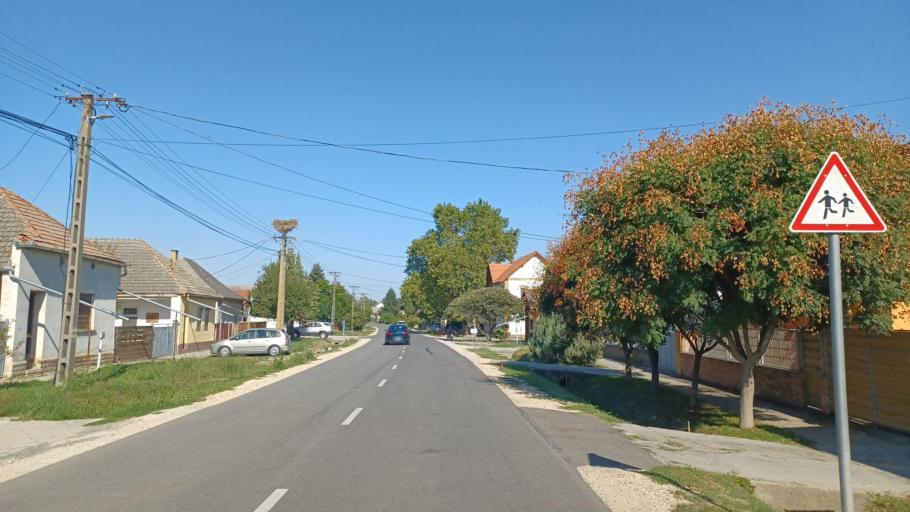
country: HU
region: Tolna
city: Nemetker
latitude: 46.7191
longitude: 18.7623
